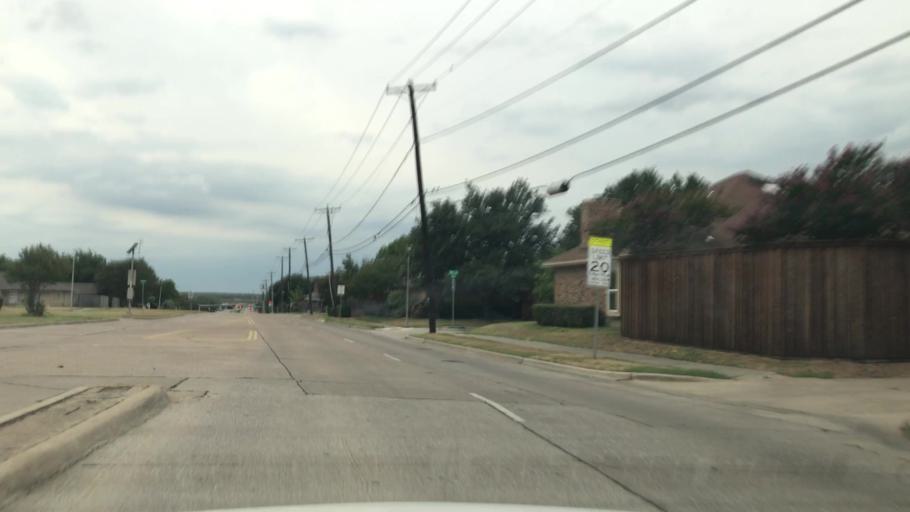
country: US
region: Texas
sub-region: Dallas County
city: Carrollton
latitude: 32.9685
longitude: -96.9077
